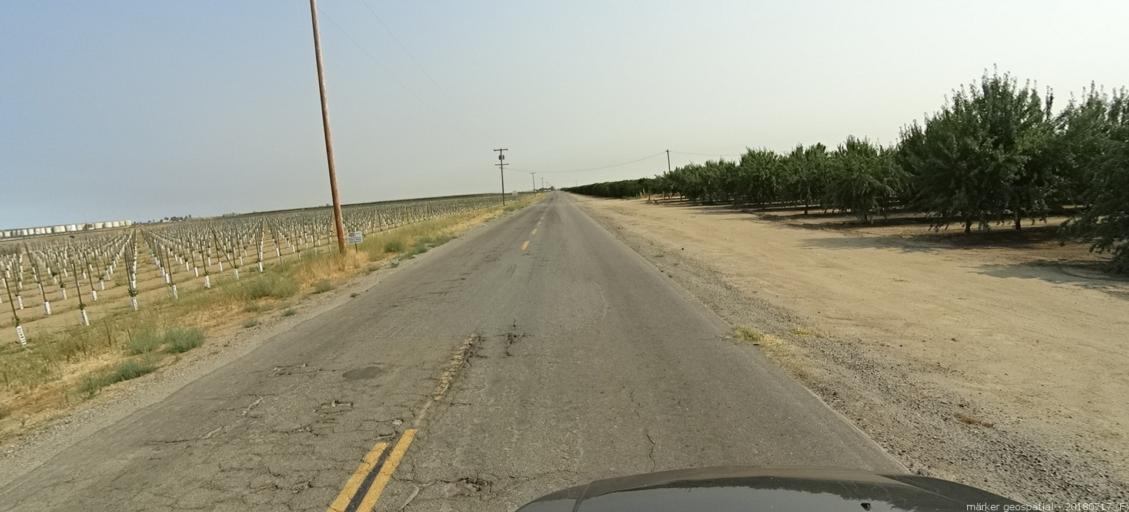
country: US
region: California
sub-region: Madera County
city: Madera Acres
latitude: 37.0717
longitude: -120.1108
